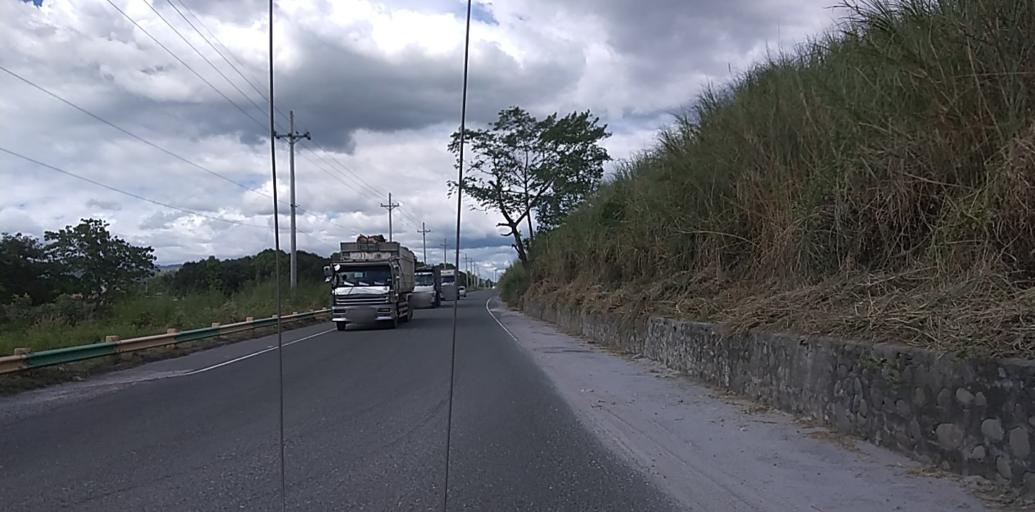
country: PH
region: Central Luzon
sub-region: Province of Pampanga
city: Dolores
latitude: 15.1000
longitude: 120.5245
